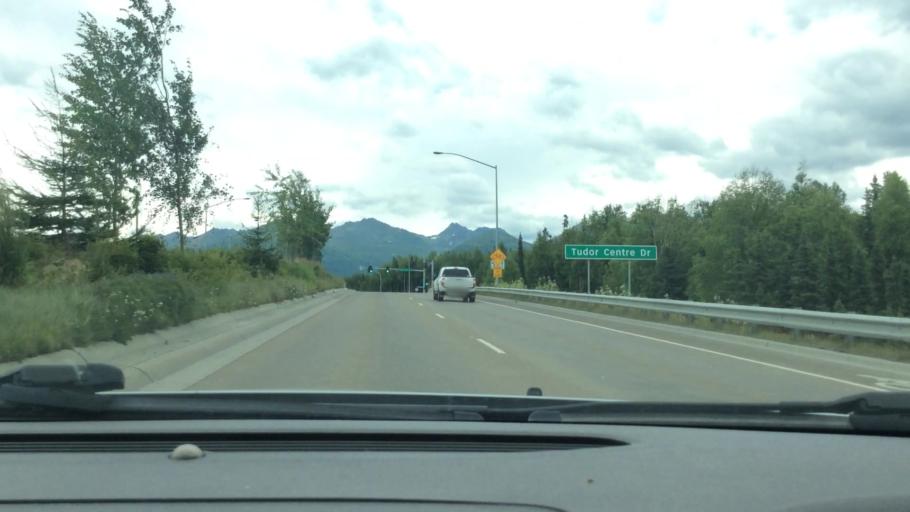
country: US
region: Alaska
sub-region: Anchorage Municipality
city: Anchorage
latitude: 61.1781
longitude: -149.7983
